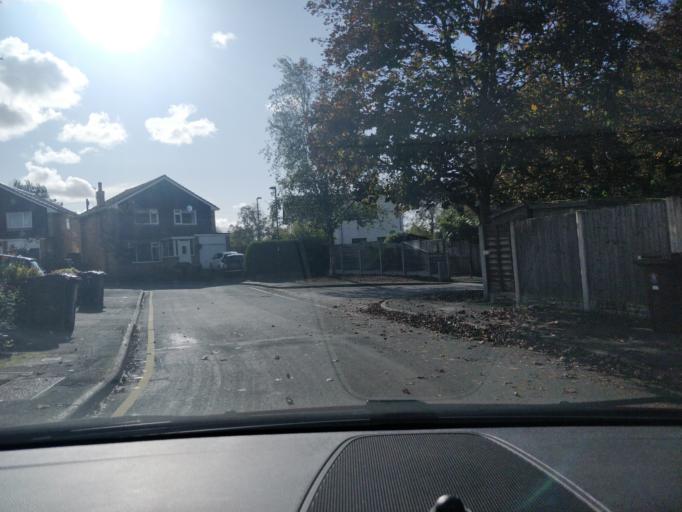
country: GB
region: England
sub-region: Lancashire
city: Ormskirk
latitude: 53.5717
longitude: -2.8745
